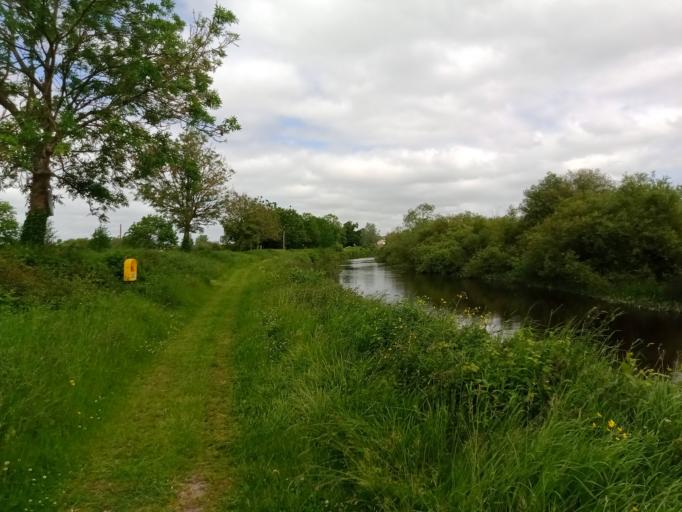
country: IE
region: Leinster
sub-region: County Carlow
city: Carlow
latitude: 52.8074
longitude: -6.9670
